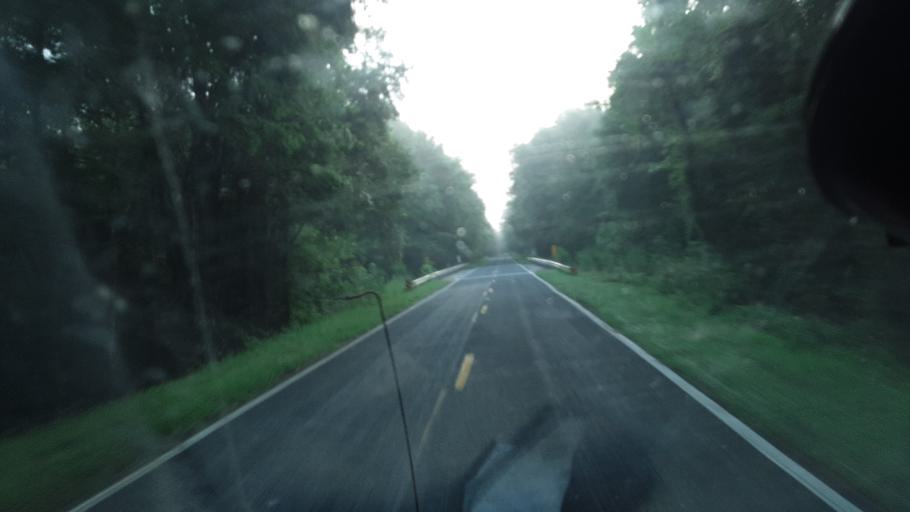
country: US
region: South Carolina
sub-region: Clarendon County
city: Manning
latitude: 33.7564
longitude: -80.0612
